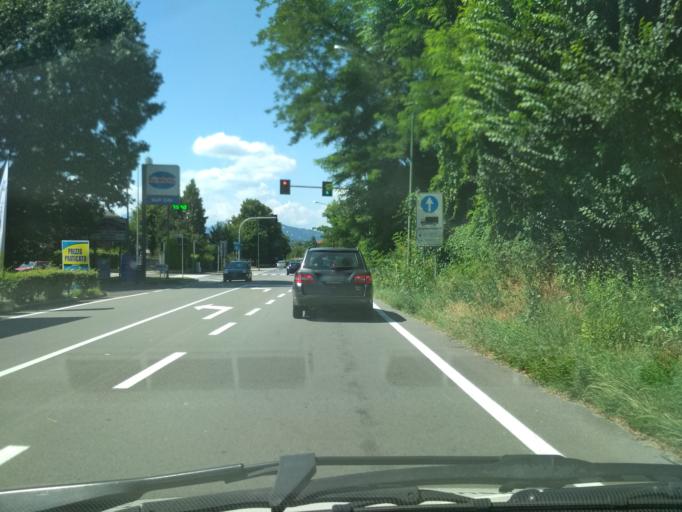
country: IT
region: Piedmont
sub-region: Provincia di Torino
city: Rivalta di Torino
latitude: 45.0339
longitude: 7.5251
